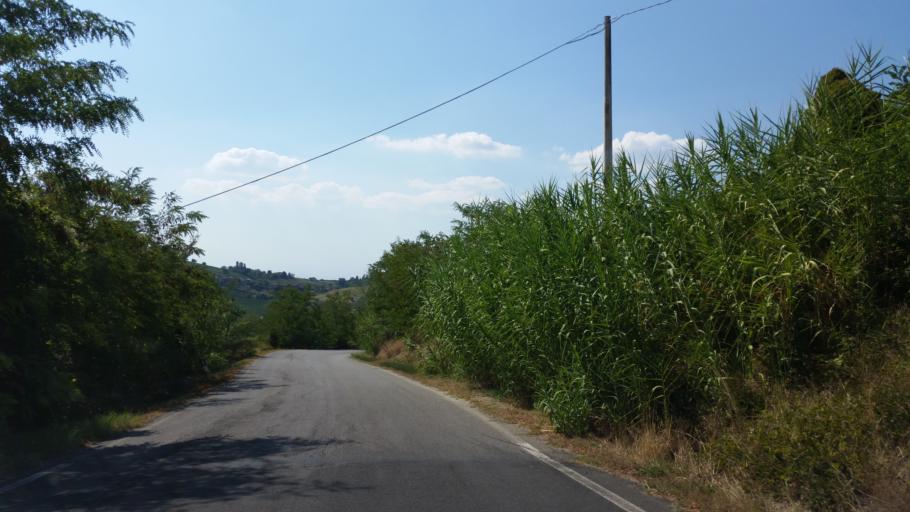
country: IT
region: Piedmont
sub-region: Provincia di Cuneo
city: Treiso
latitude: 44.6889
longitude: 8.0712
